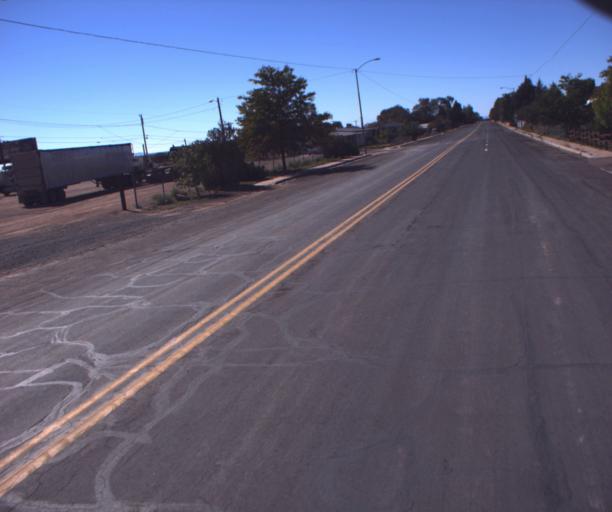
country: US
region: Arizona
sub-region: Navajo County
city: Joseph City
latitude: 34.9560
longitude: -110.3256
